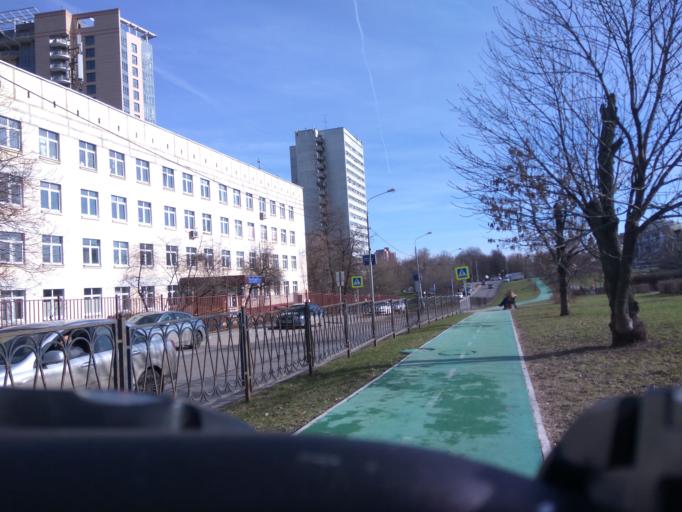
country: RU
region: Moscow
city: Davydkovo
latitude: 55.7220
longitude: 37.4618
